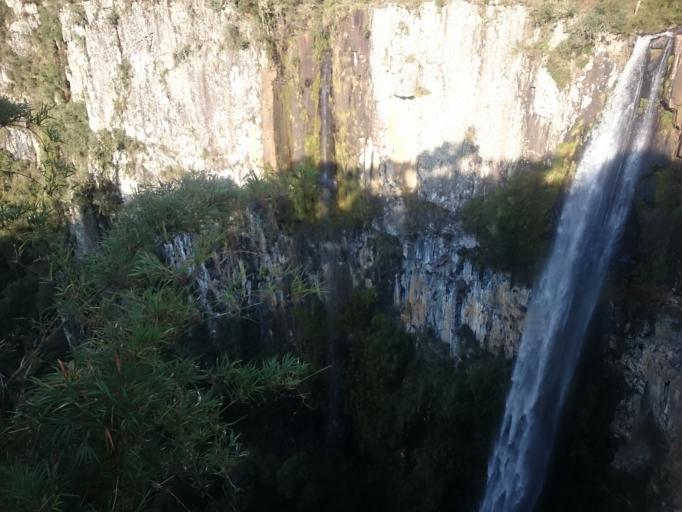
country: BR
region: Santa Catarina
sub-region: Sao Joaquim
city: Sao Joaquim
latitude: -28.0467
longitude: -49.6177
